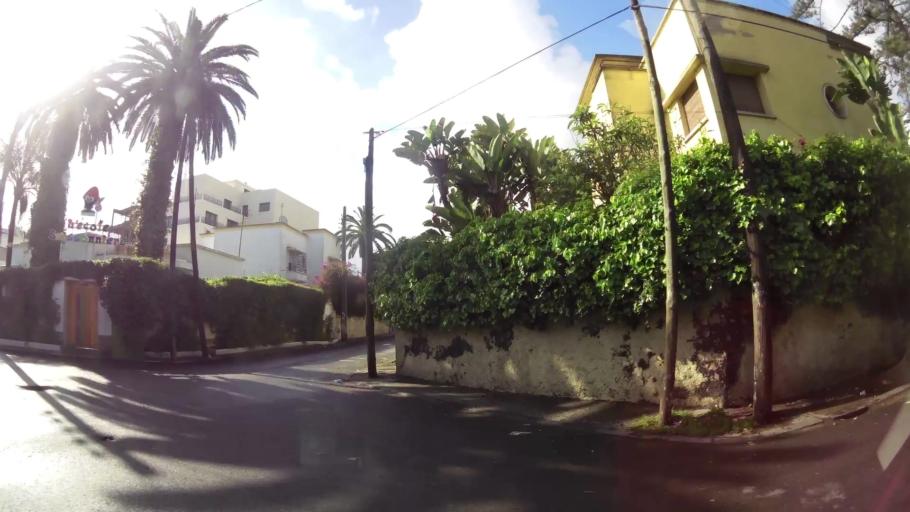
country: MA
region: Grand Casablanca
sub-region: Casablanca
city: Casablanca
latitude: 33.5802
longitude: -7.6281
